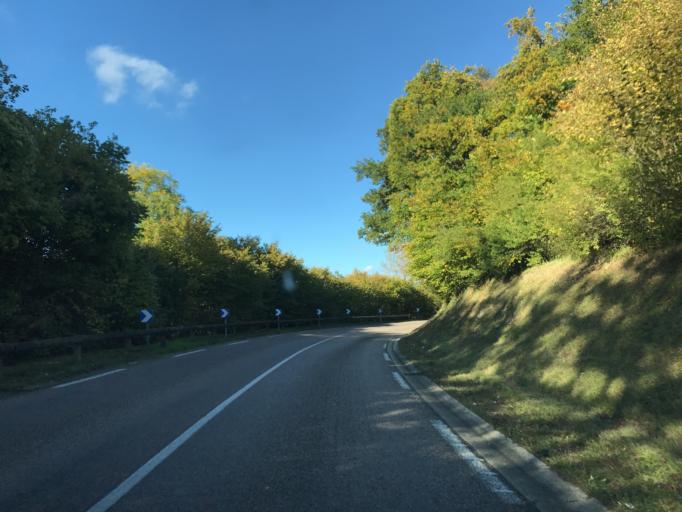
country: FR
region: Haute-Normandie
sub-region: Departement de l'Eure
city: Saint-Aubin-sur-Gaillon
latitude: 49.1043
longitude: 1.2918
